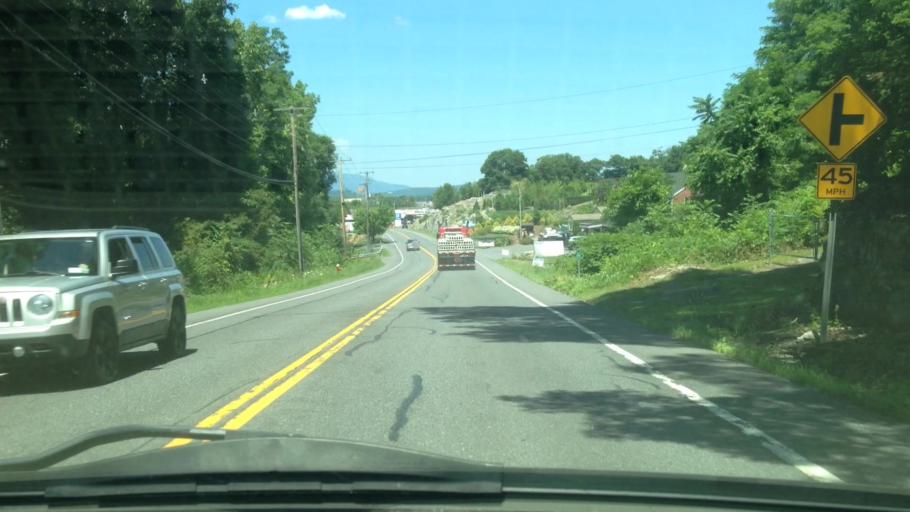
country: US
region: New York
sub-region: Ulster County
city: Lincoln Park
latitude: 41.9523
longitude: -73.9909
